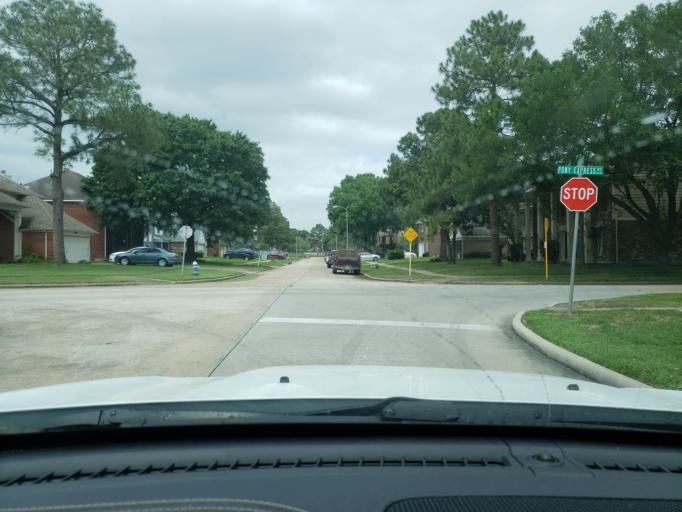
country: US
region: Texas
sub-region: Harris County
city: Jersey Village
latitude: 29.9210
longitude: -95.5716
